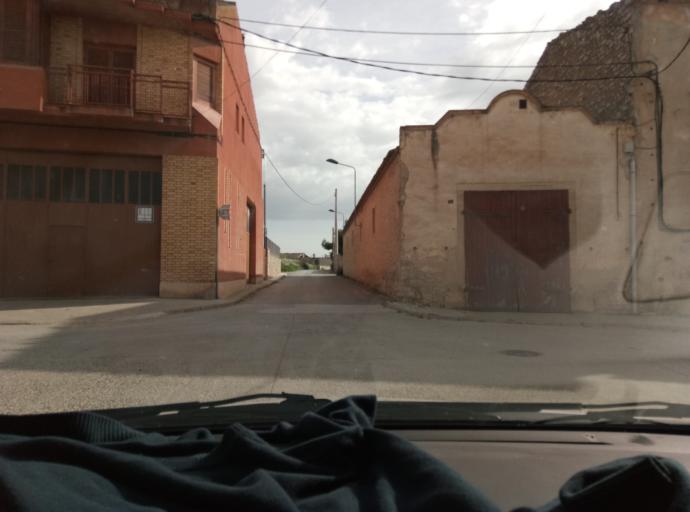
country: ES
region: Catalonia
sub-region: Provincia de Lleida
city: Verdu
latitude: 41.6090
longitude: 1.1430
